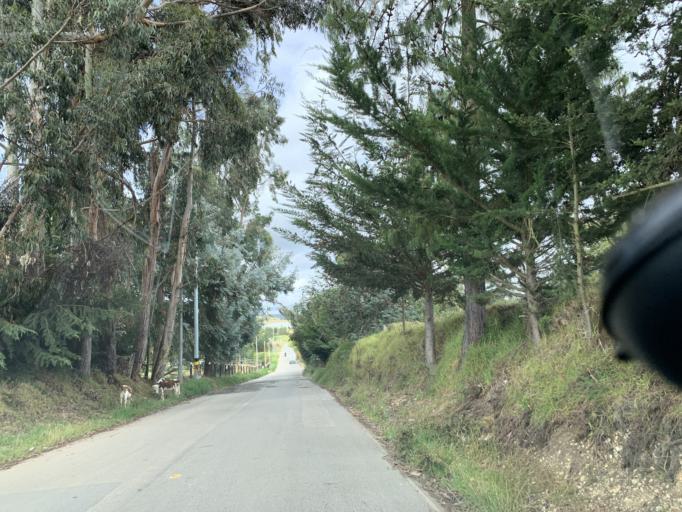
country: CO
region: Boyaca
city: Toca
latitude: 5.5678
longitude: -73.1977
